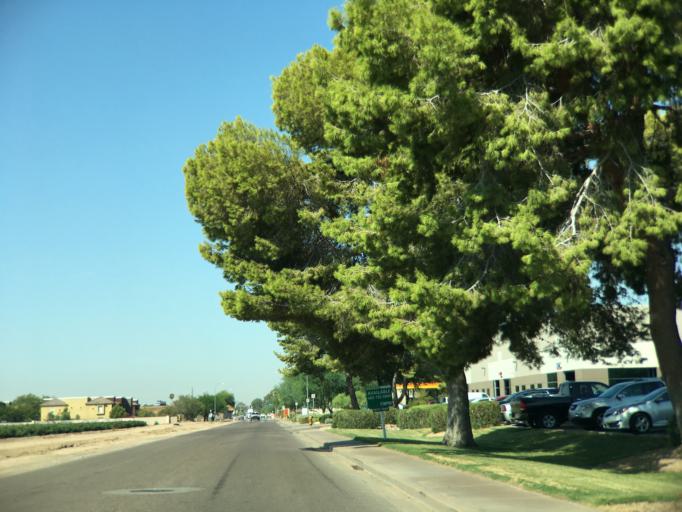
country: US
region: Arizona
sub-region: Maricopa County
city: Glendale
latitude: 33.4588
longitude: -112.1793
